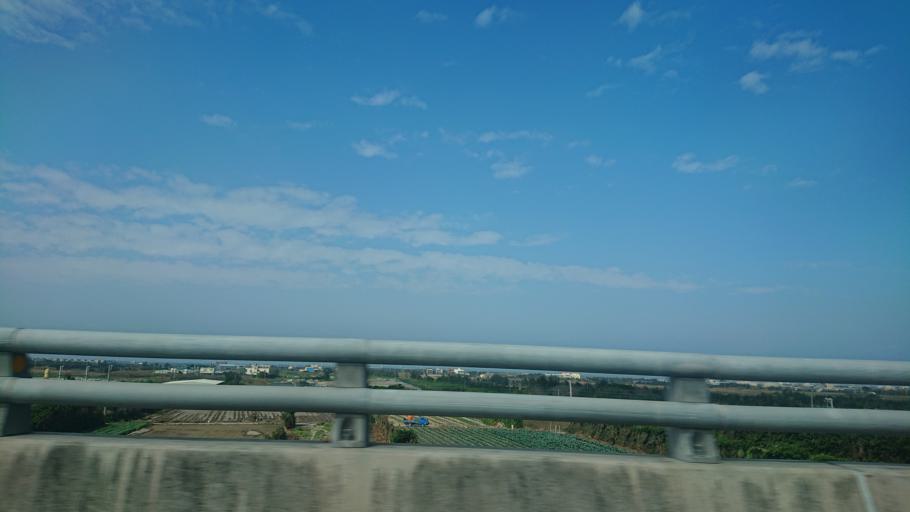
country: TW
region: Taiwan
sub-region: Changhua
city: Chang-hua
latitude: 23.9798
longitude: 120.3639
